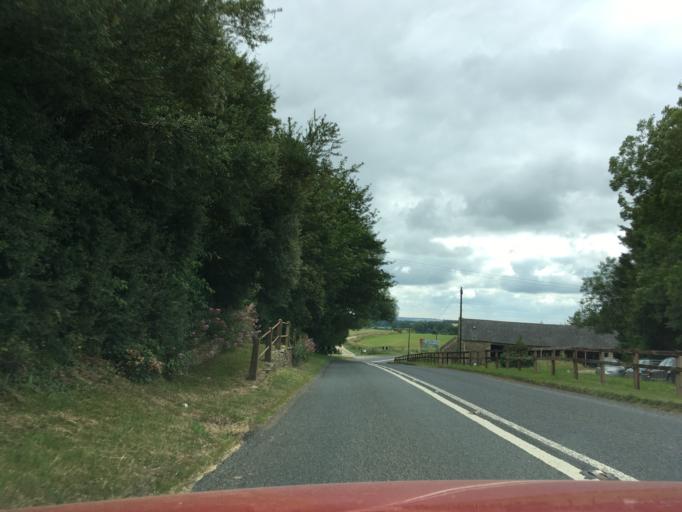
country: GB
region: England
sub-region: Gloucestershire
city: Westfield
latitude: 51.8936
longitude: -1.8756
